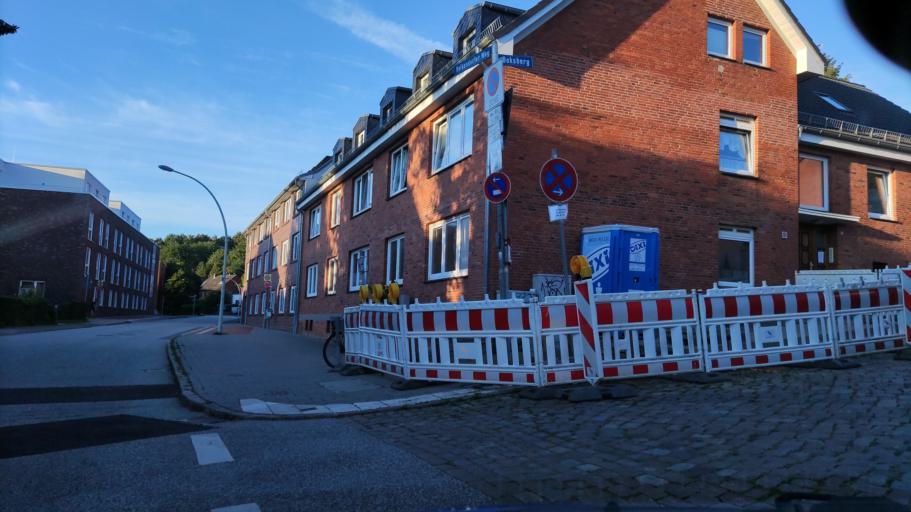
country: DE
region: Schleswig-Holstein
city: Monkeberg
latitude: 54.3321
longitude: 10.1826
